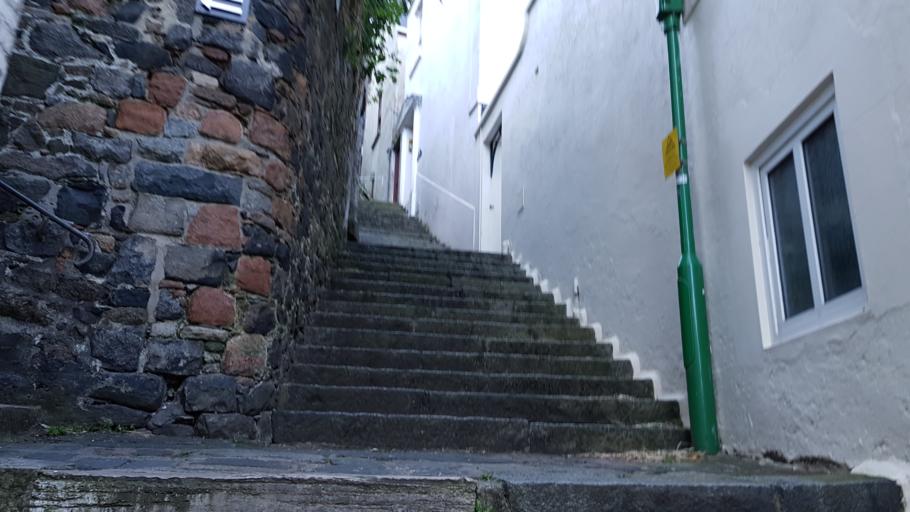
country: GG
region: St Peter Port
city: Saint Peter Port
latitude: 49.4543
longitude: -2.5381
